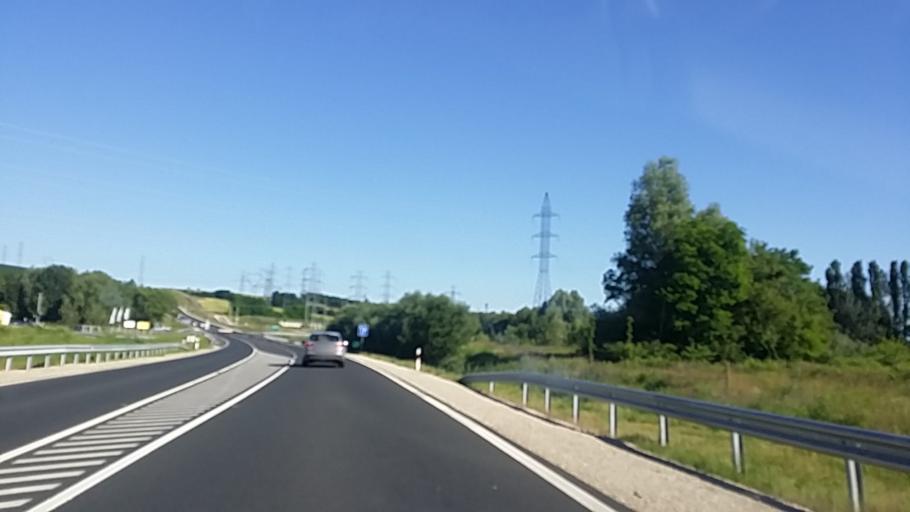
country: HU
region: Zala
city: Heviz
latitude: 46.7867
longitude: 17.1743
